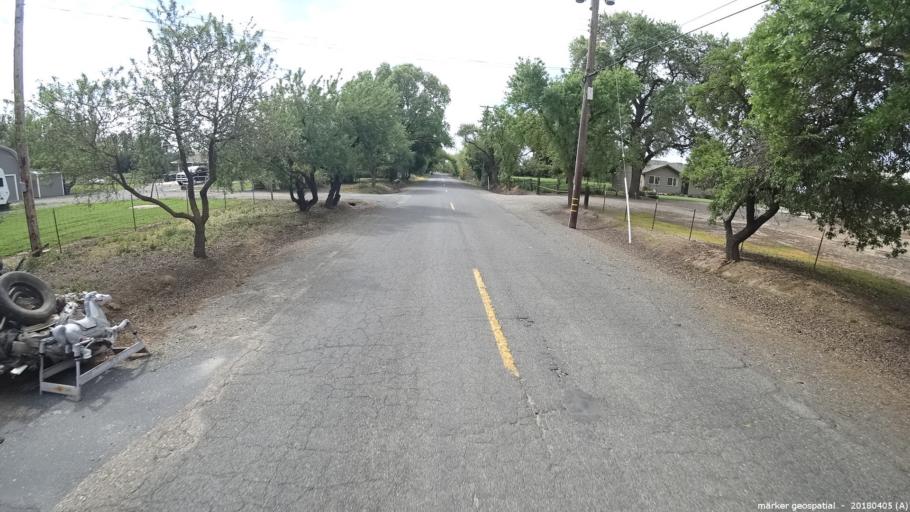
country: US
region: California
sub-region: Sacramento County
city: Galt
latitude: 38.2492
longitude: -121.3373
